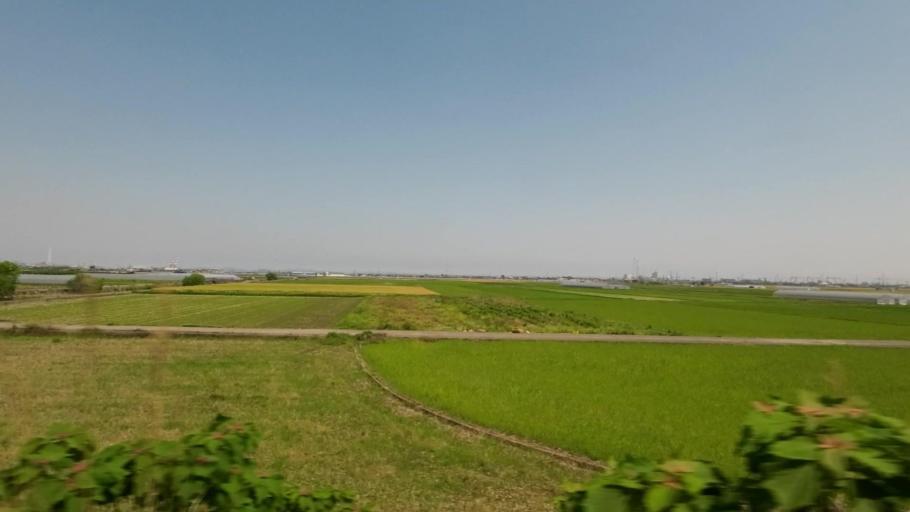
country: JP
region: Ehime
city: Saijo
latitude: 33.8959
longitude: 133.1517
